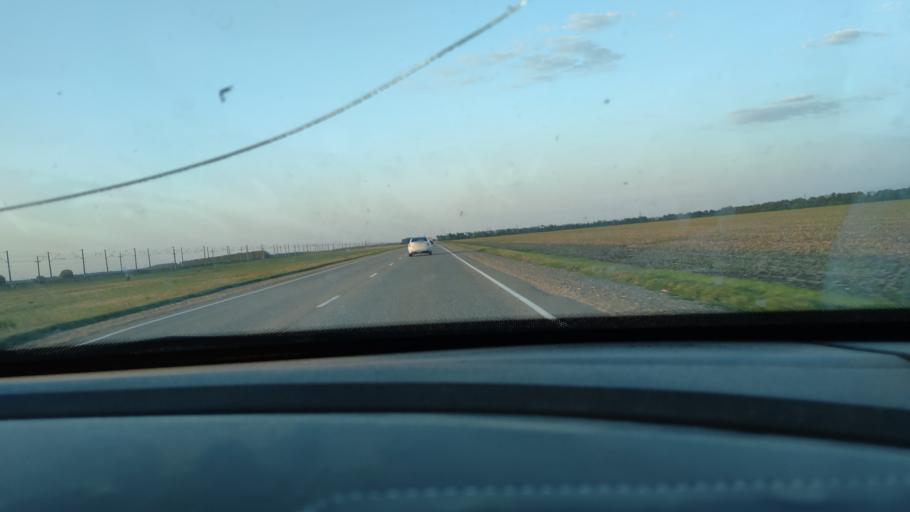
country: RU
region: Krasnodarskiy
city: Novominskaya
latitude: 46.3796
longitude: 38.9817
